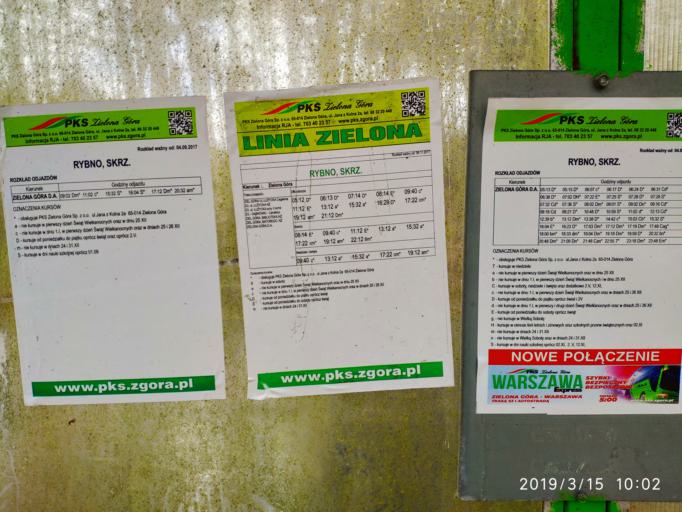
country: PL
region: Lubusz
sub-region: Zielona Gora
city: Zielona Gora
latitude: 51.9268
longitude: 15.4603
